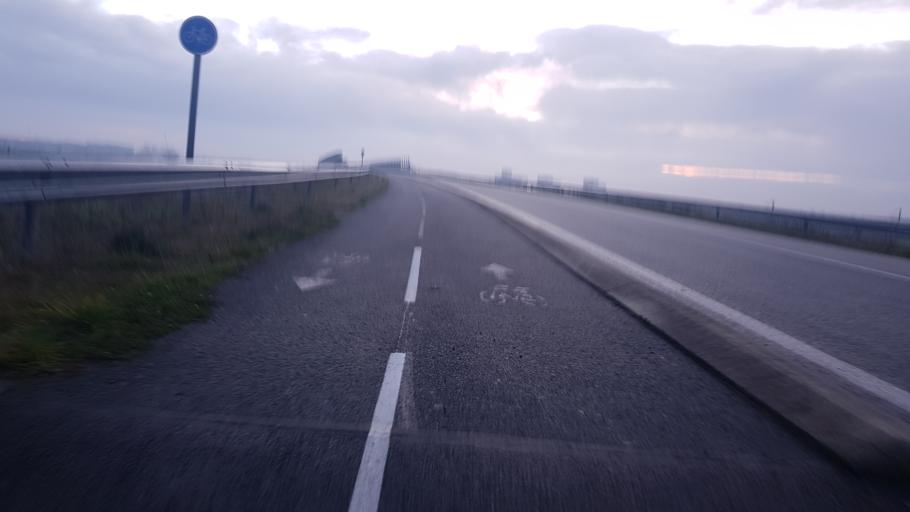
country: FR
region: Poitou-Charentes
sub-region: Departement de la Vienne
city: Chasseneuil-du-Poitou
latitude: 46.6569
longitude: 0.3508
